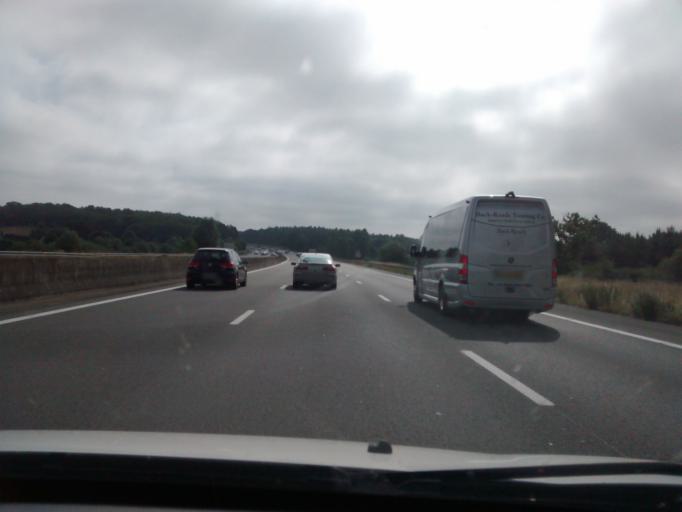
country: FR
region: Pays de la Loire
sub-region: Departement de la Sarthe
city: Connerre
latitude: 48.0748
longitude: 0.4668
